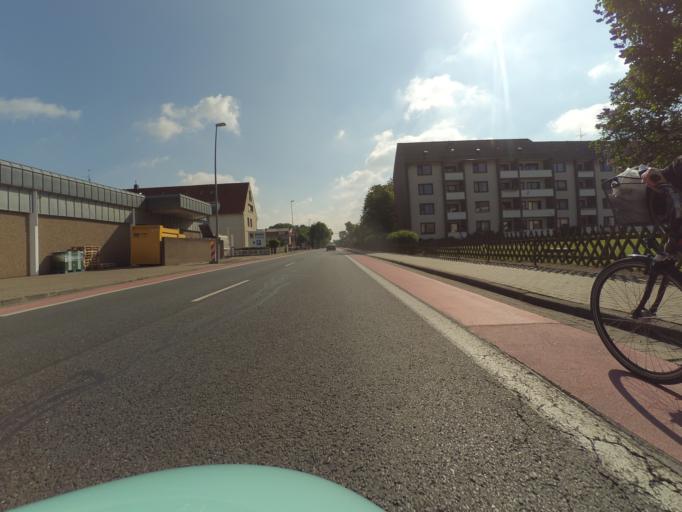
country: DE
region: Lower Saxony
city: Burgdorf
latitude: 52.4441
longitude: 10.0154
